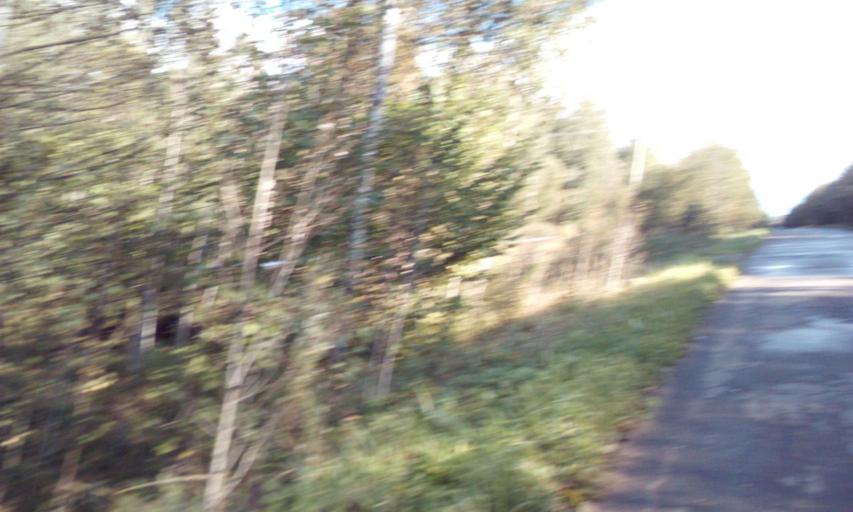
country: RU
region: Moskovskaya
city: Kievskij
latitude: 55.3890
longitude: 36.9022
